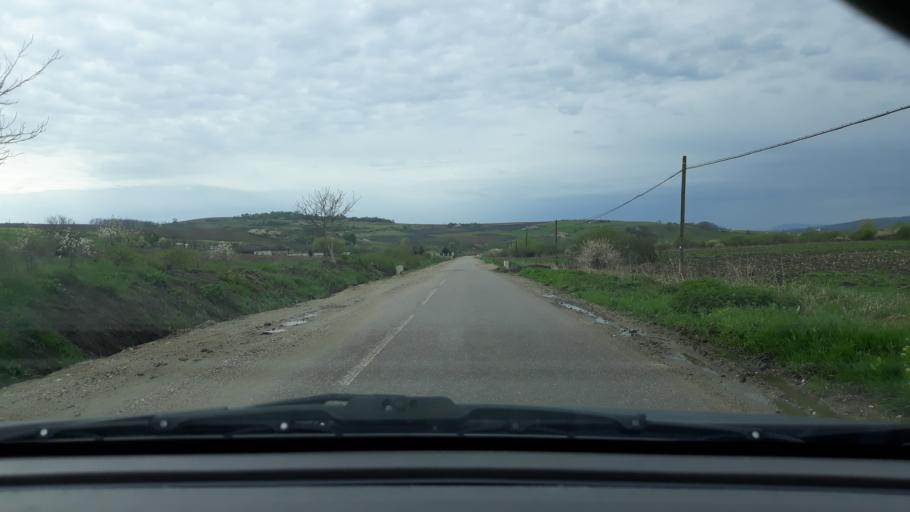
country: RO
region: Salaj
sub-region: Comuna Cehu Silvaniei
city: Cehu Silvaniei
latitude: 47.3967
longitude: 23.1532
